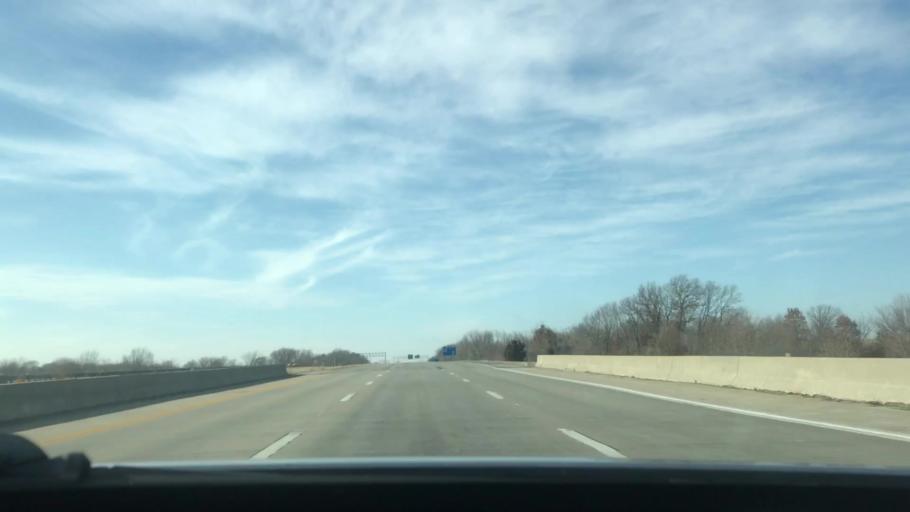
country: US
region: Missouri
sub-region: Platte County
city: Weatherby Lake
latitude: 39.3077
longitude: -94.6489
